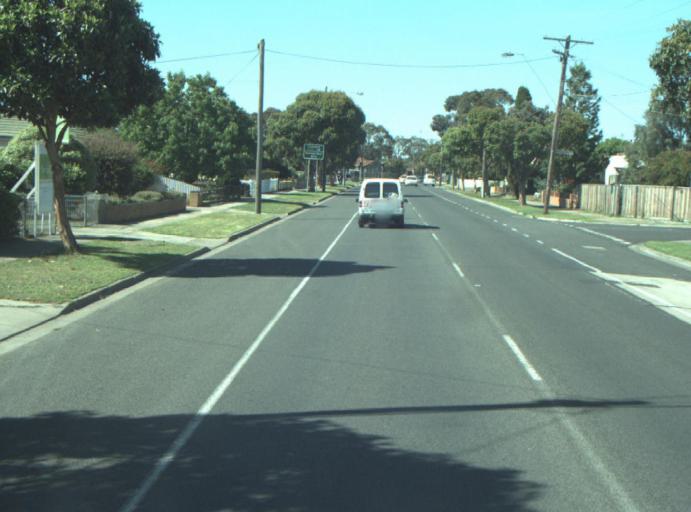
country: AU
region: Victoria
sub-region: Greater Geelong
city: Hamlyn Heights
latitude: -38.1267
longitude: 144.3272
